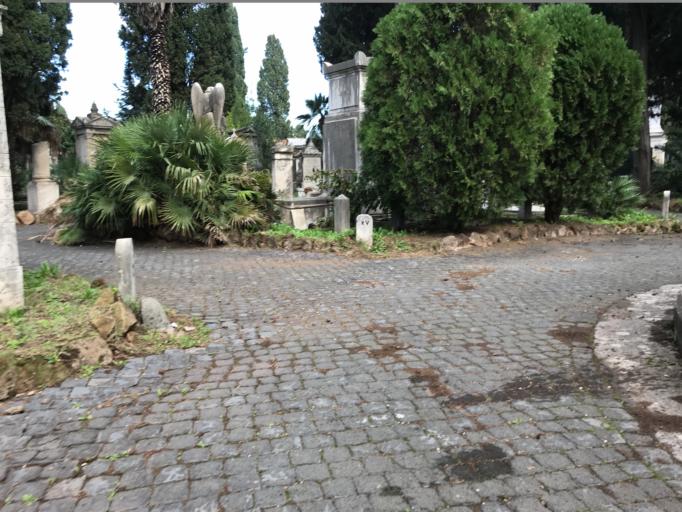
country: IT
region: Latium
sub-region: Citta metropolitana di Roma Capitale
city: Rome
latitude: 41.9031
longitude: 12.5208
